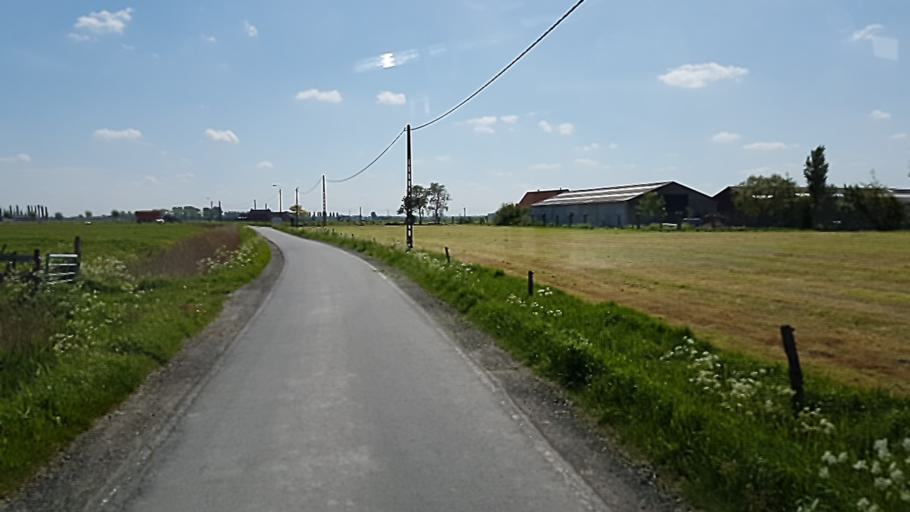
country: BE
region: Flanders
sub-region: Provincie West-Vlaanderen
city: De Haan
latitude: 51.2570
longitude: 3.0434
